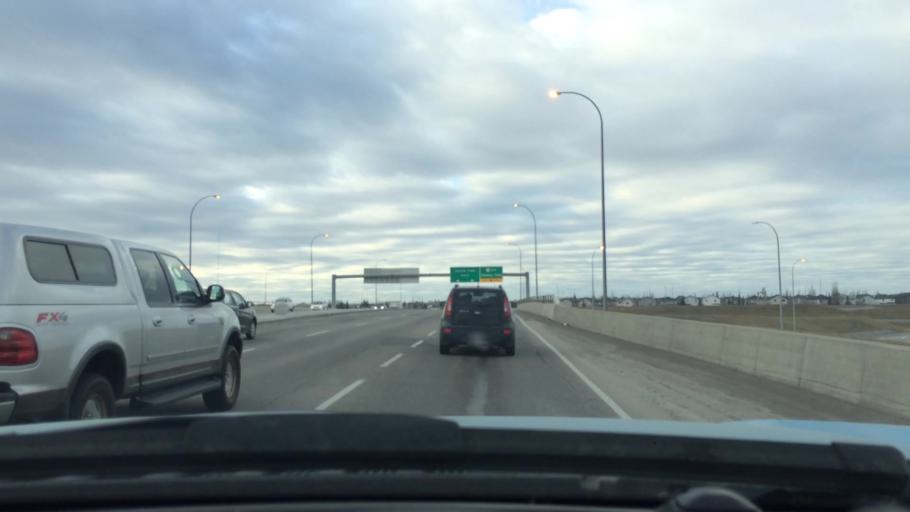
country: CA
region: Alberta
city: Calgary
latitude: 51.1529
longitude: -114.1651
